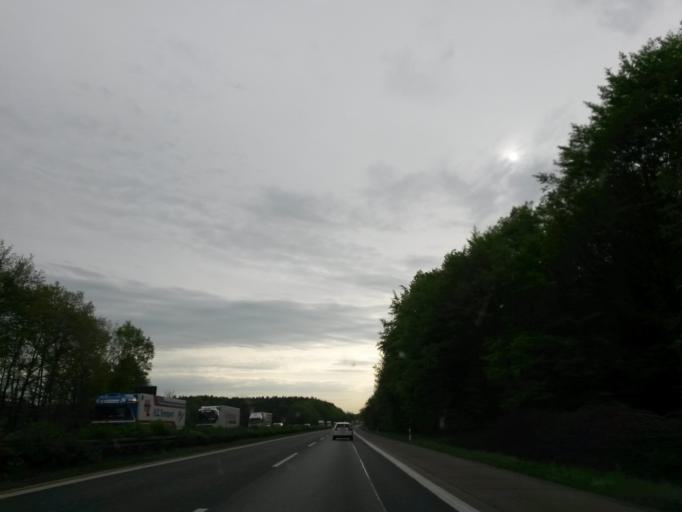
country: DE
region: Bavaria
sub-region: Regierungsbezirk Mittelfranken
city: Muhlhausen
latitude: 49.7348
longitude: 10.7495
